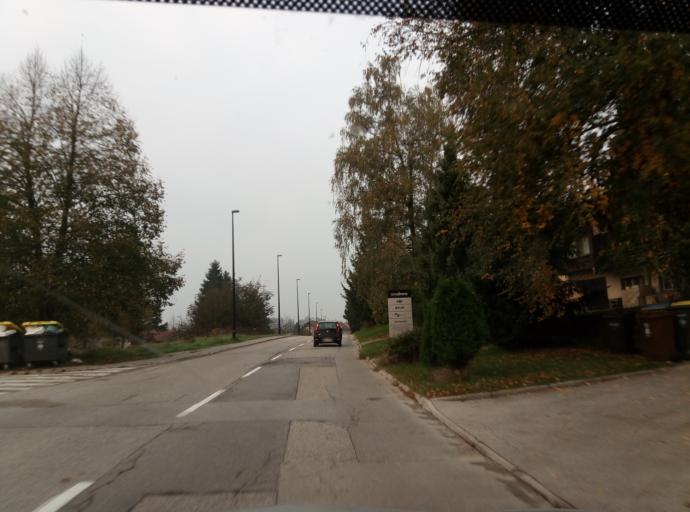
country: SI
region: Ljubljana
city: Ljubljana
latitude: 46.0881
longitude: 14.4671
